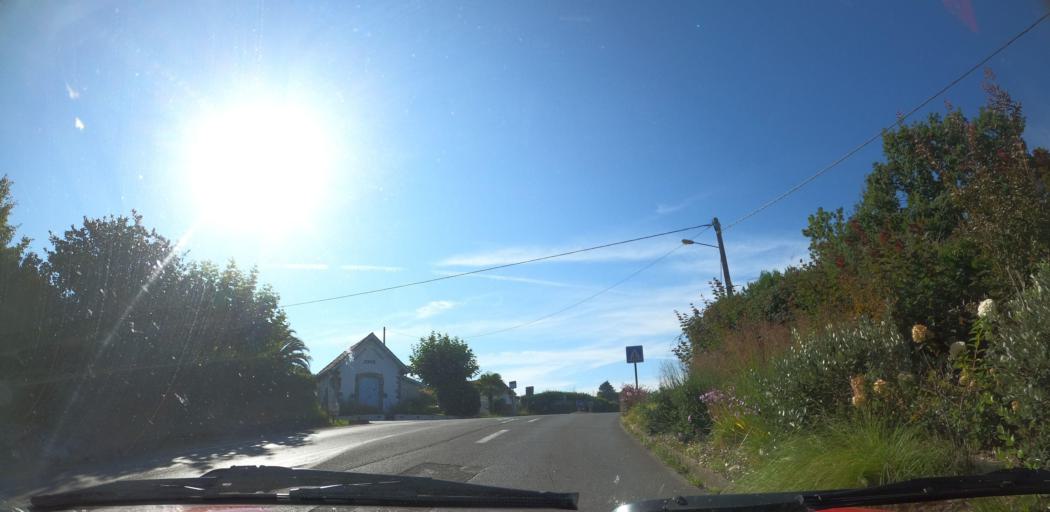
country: FR
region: Aquitaine
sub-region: Departement des Pyrenees-Atlantiques
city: Arbonne
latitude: 43.4284
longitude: -1.5492
